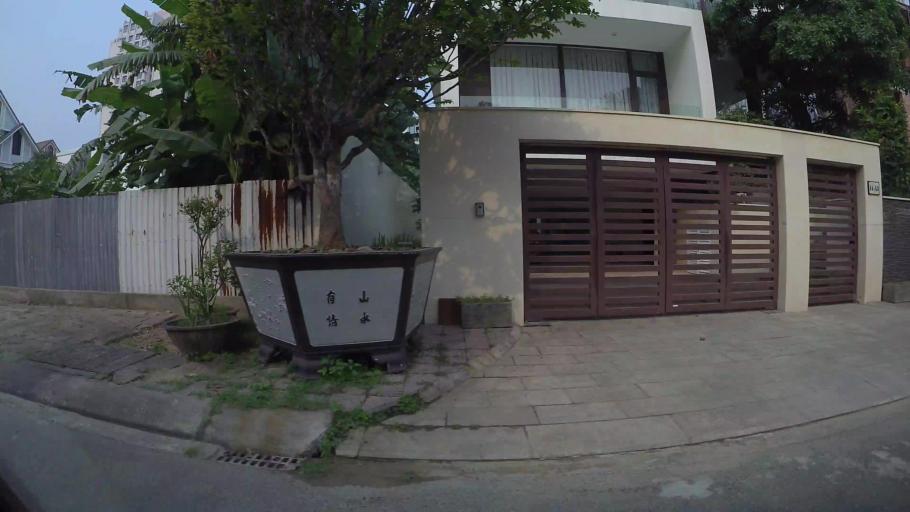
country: VN
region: Da Nang
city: Son Tra
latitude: 16.0466
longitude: 108.2263
